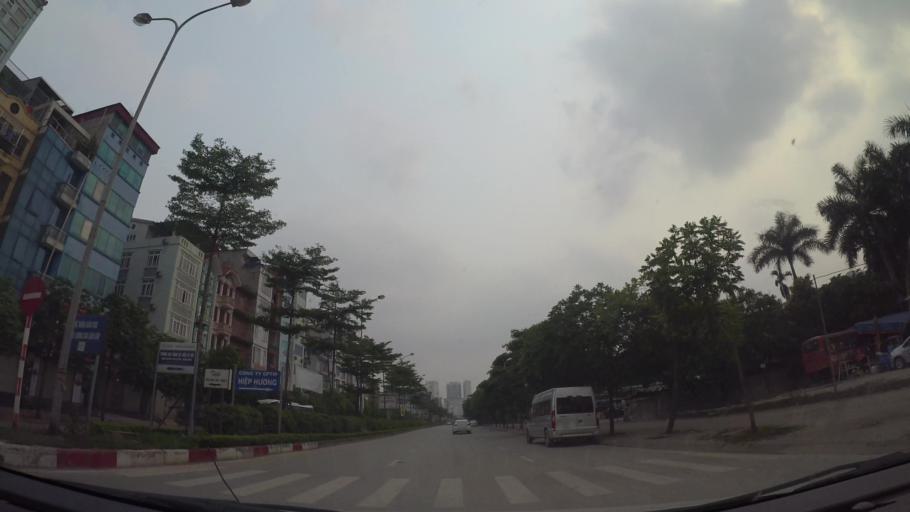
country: VN
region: Ha Noi
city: Cau Dien
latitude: 21.0449
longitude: 105.7743
